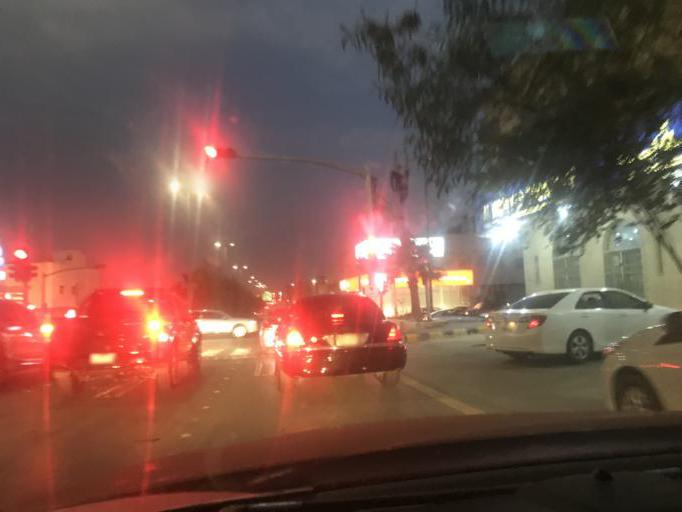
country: SA
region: Ar Riyad
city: Riyadh
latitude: 24.7314
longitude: 46.7618
